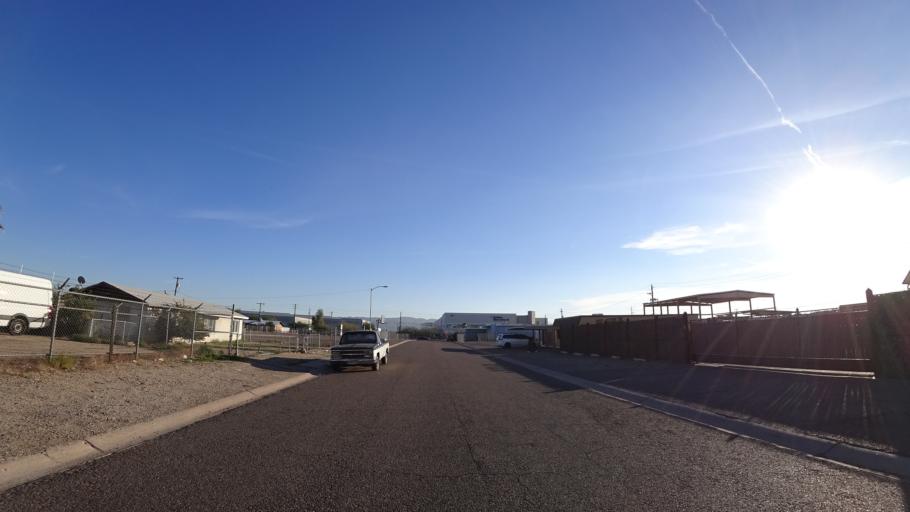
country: US
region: Arizona
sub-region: Maricopa County
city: Phoenix
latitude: 33.4251
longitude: -112.0414
